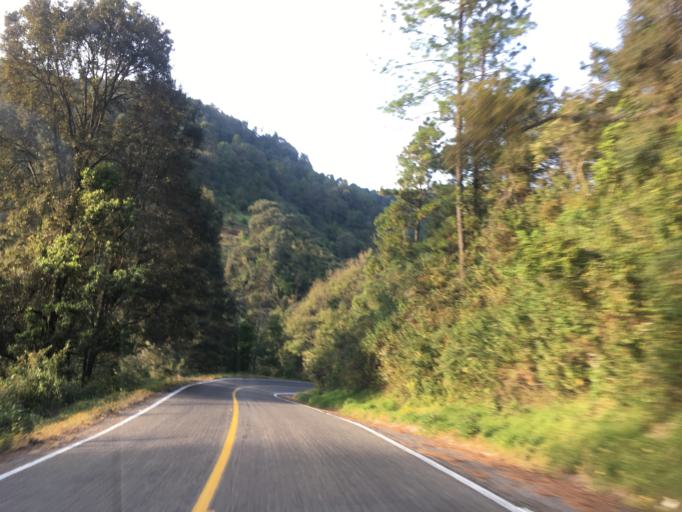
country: MX
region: Michoacan
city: Tzitzio
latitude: 19.6706
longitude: -100.9168
